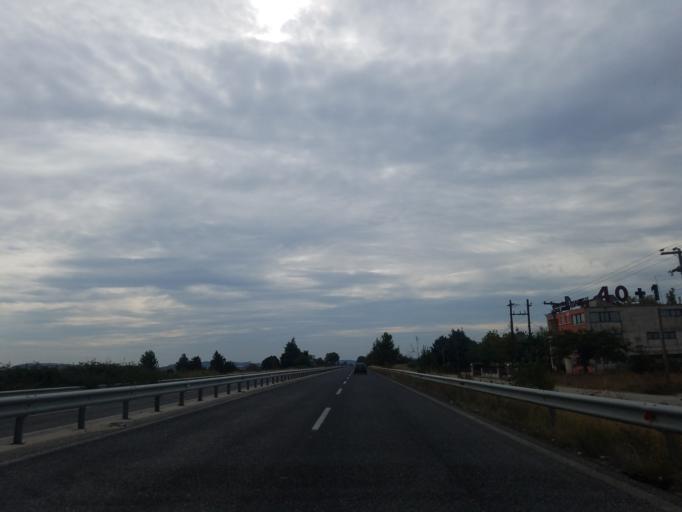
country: GR
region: Thessaly
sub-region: Trikala
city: Vasiliki
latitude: 39.6244
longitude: 21.7090
